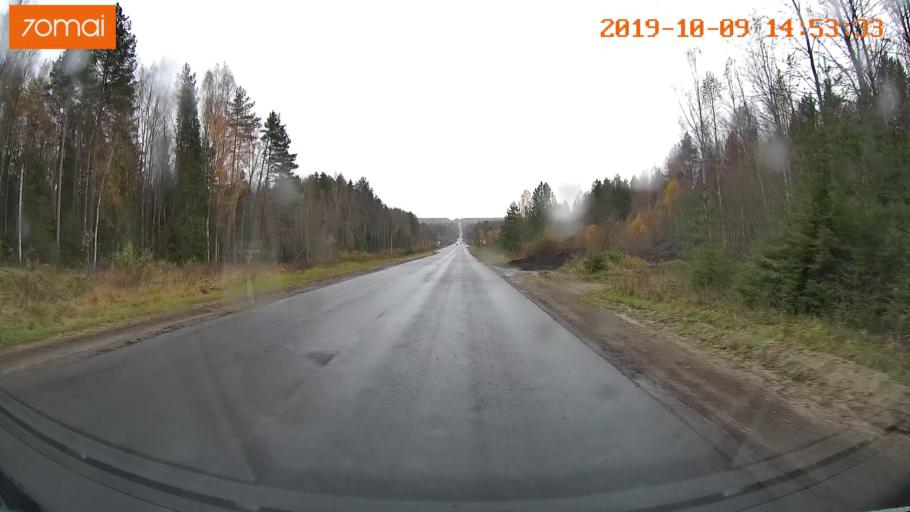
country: RU
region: Kostroma
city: Chistyye Bory
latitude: 58.3665
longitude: 41.6388
